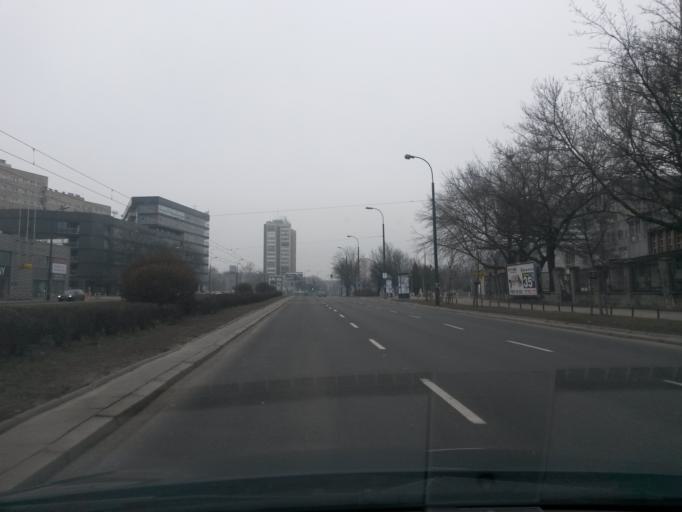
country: PL
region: Masovian Voivodeship
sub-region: Warszawa
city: Wola
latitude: 52.2339
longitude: 20.9820
